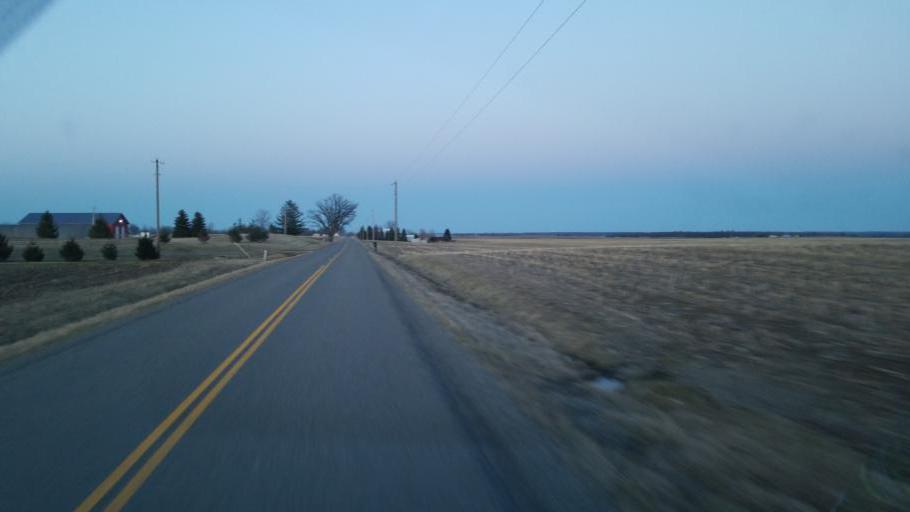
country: US
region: Ohio
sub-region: Champaign County
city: North Lewisburg
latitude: 40.2406
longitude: -83.6094
